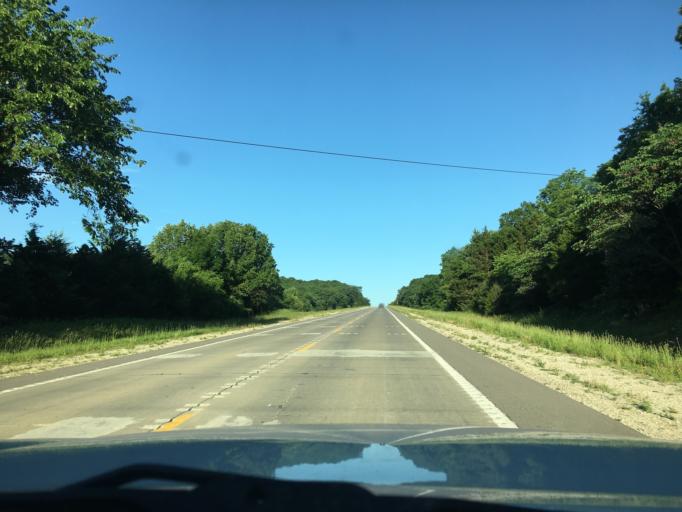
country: US
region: Missouri
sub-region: Gasconade County
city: Owensville
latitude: 38.4819
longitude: -91.5568
